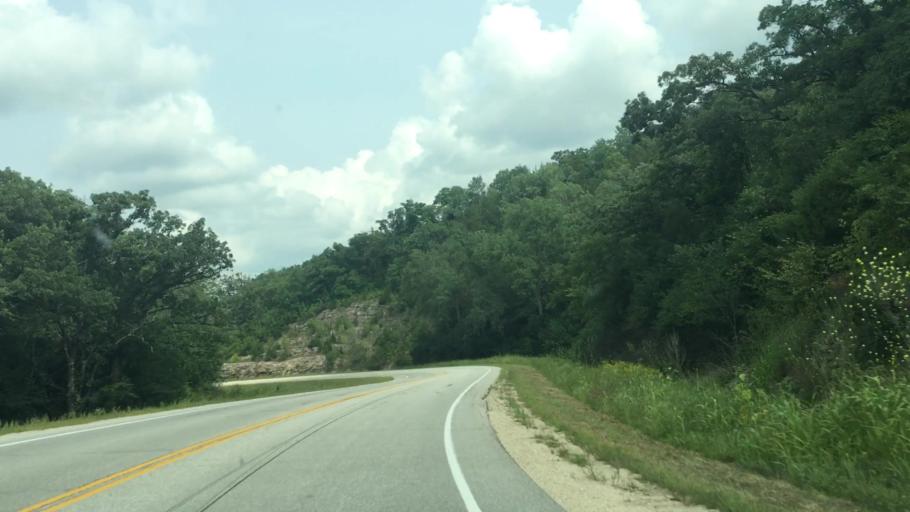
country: US
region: Minnesota
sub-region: Fillmore County
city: Preston
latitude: 43.7028
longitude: -91.9700
